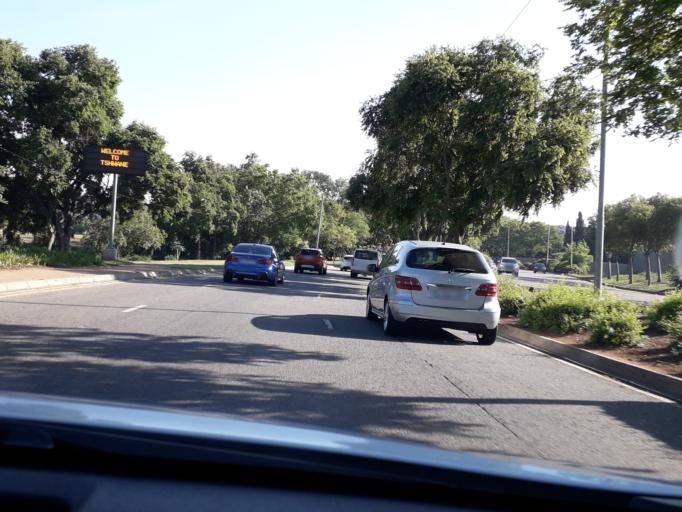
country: ZA
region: Gauteng
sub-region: City of Tshwane Metropolitan Municipality
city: Pretoria
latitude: -25.7607
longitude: 28.1950
